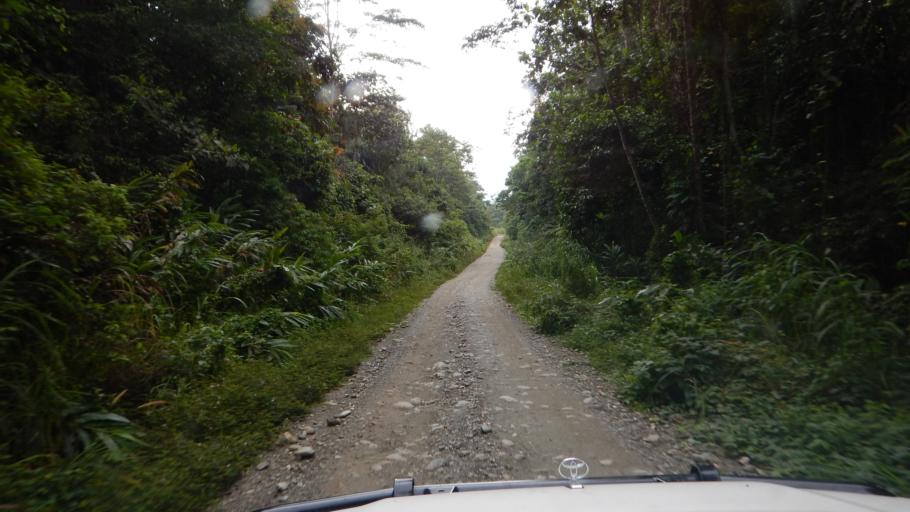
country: PG
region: Northern Province
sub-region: Sohe
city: Kokoda
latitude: -8.9066
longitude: 147.8219
